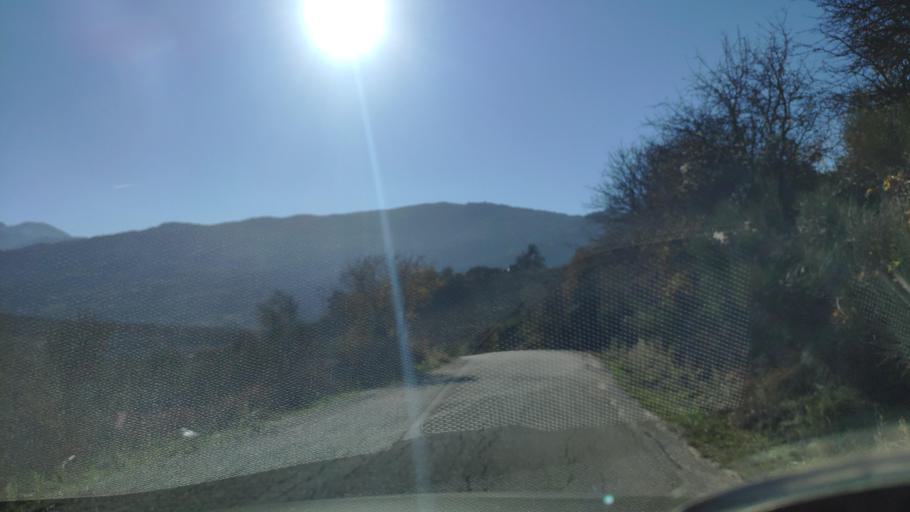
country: GR
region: Peloponnese
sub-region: Nomos Korinthias
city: Xylokastro
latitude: 38.0306
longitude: 22.4746
